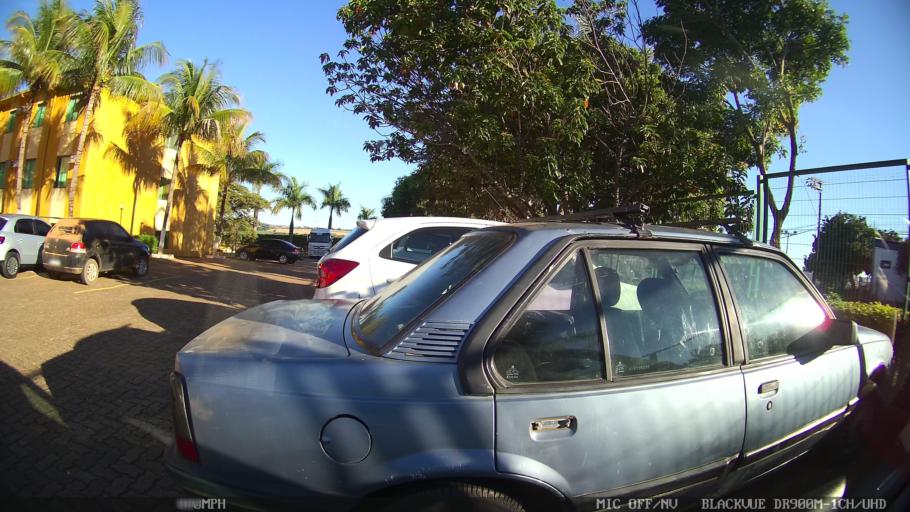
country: BR
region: Sao Paulo
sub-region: Franca
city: Franca
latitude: -20.5622
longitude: -47.4101
